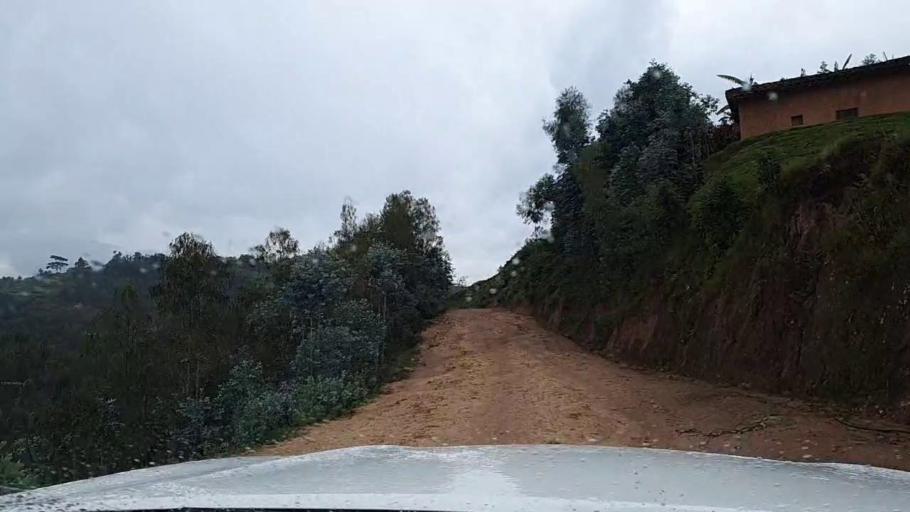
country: RW
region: Southern Province
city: Nzega
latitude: -2.4621
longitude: 29.4943
